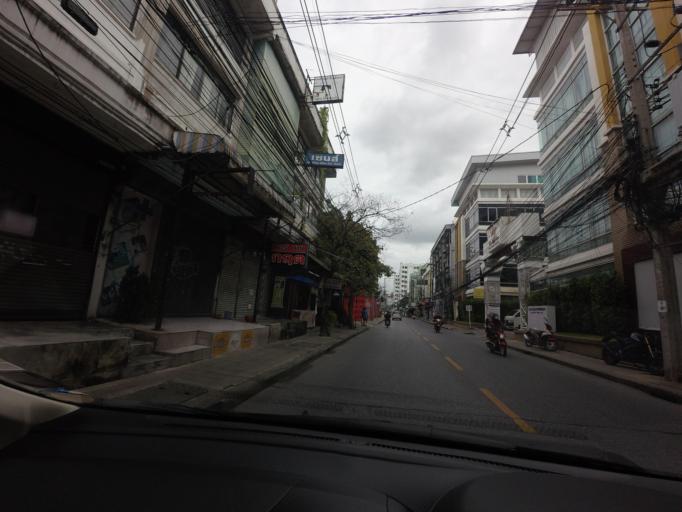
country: TH
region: Bangkok
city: Bang Kapi
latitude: 13.7648
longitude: 100.6237
